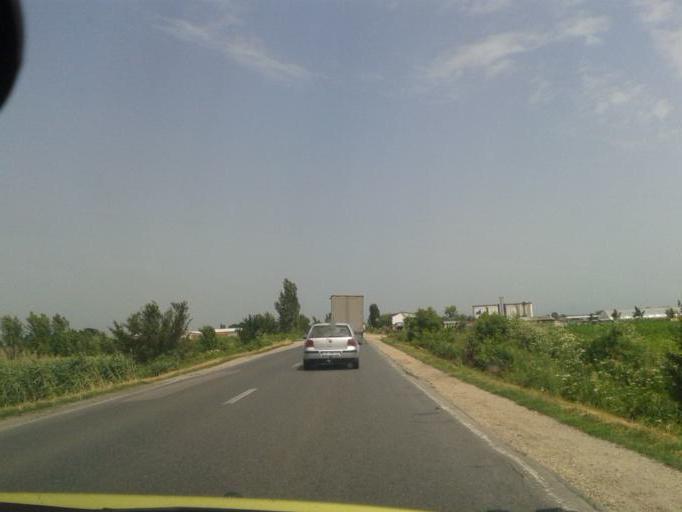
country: RO
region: Dambovita
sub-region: Oras Gaesti
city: Gaesti
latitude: 44.6981
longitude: 25.3115
